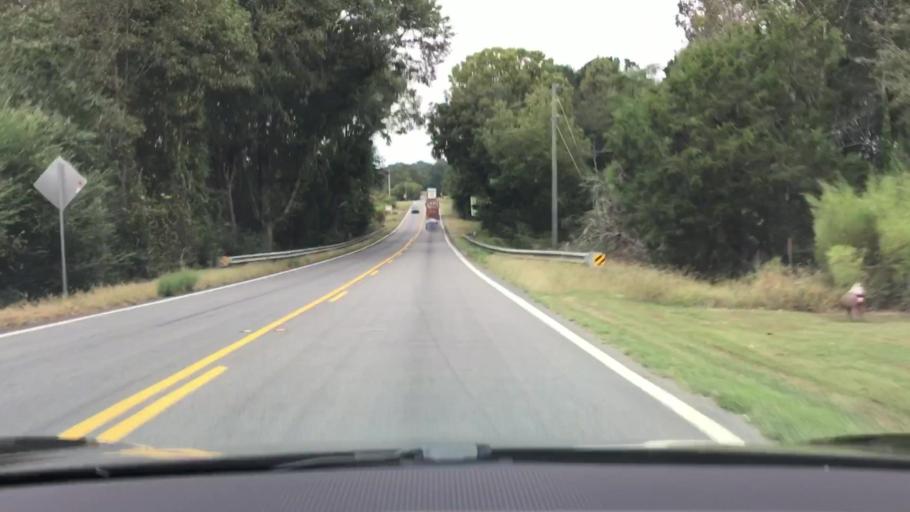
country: US
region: Georgia
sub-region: Greene County
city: Greensboro
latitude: 33.5688
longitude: -83.1626
